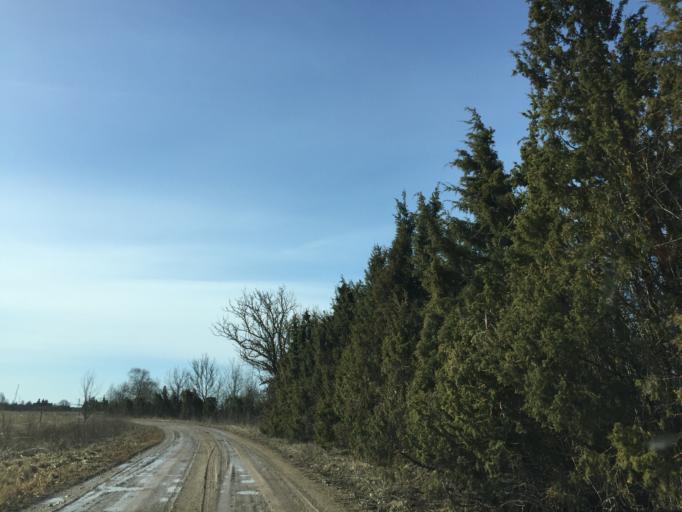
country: EE
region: Laeaene
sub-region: Haapsalu linn
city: Haapsalu
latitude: 58.6532
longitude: 23.5136
